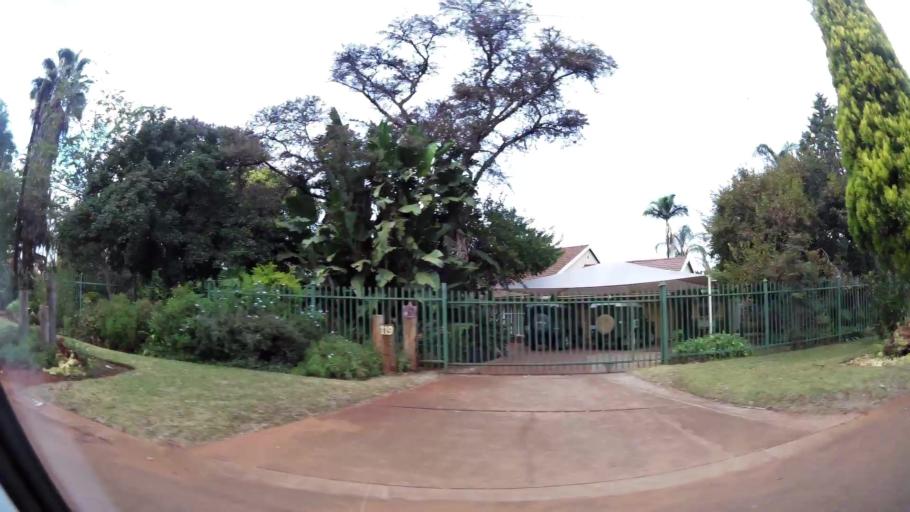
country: ZA
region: Limpopo
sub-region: Waterberg District Municipality
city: Modimolle
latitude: -24.5092
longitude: 28.7167
